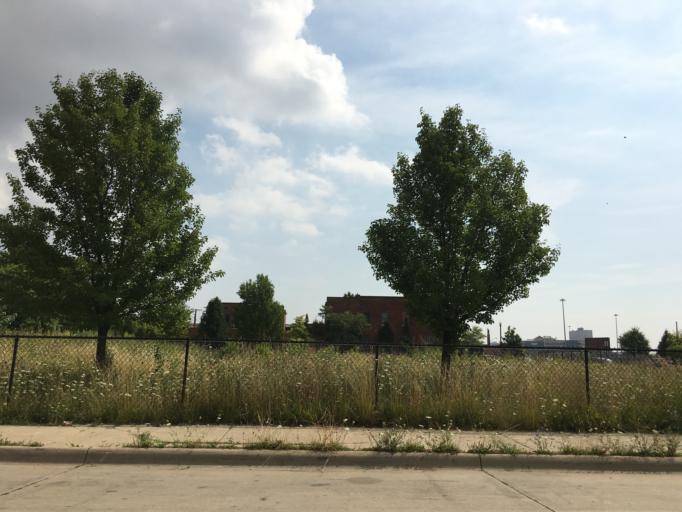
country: US
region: Michigan
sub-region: Wayne County
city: Detroit
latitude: 42.3421
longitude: -83.0513
